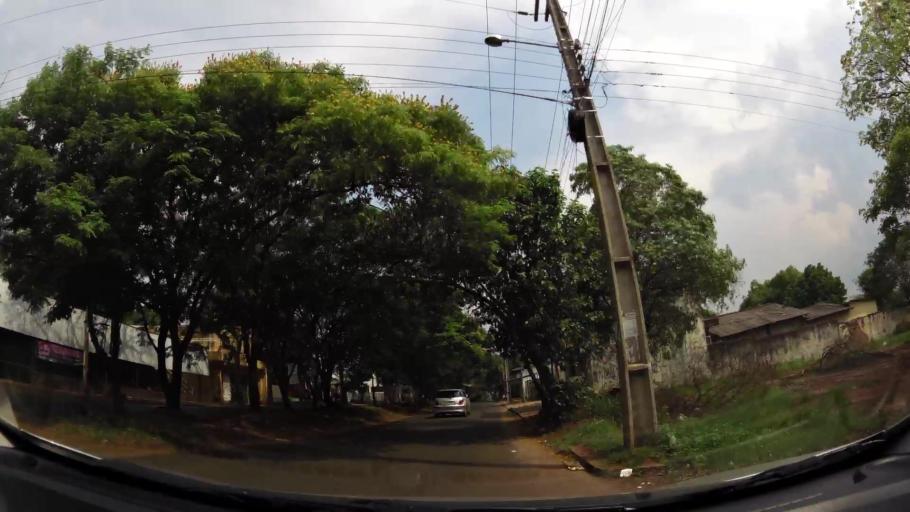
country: PY
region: Alto Parana
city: Presidente Franco
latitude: -25.5379
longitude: -54.6064
